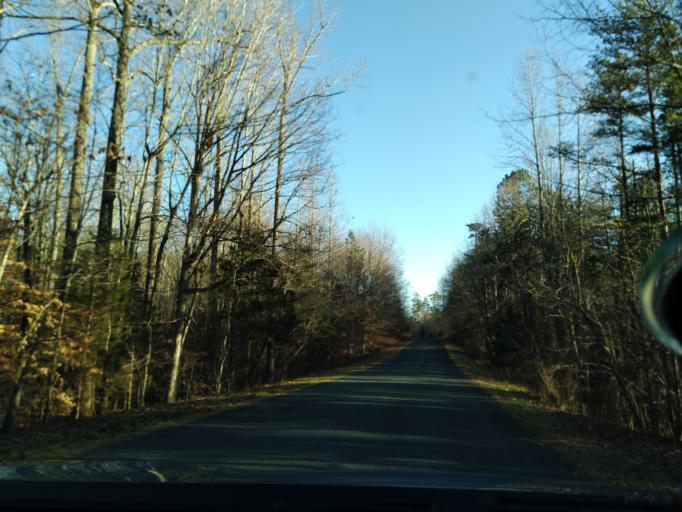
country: US
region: Virginia
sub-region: Appomattox County
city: Appomattox
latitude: 37.3867
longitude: -78.6543
